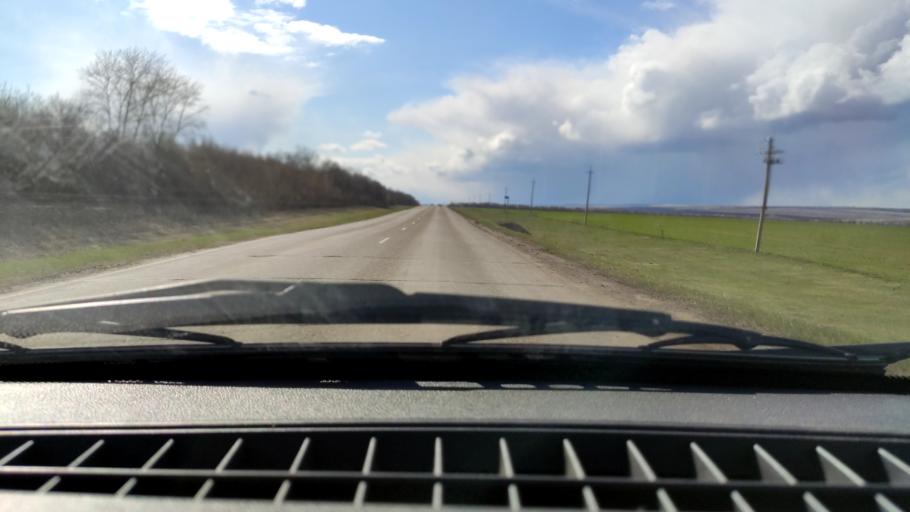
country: RU
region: Bashkortostan
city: Alekseyevka
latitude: 55.1058
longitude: 55.0010
